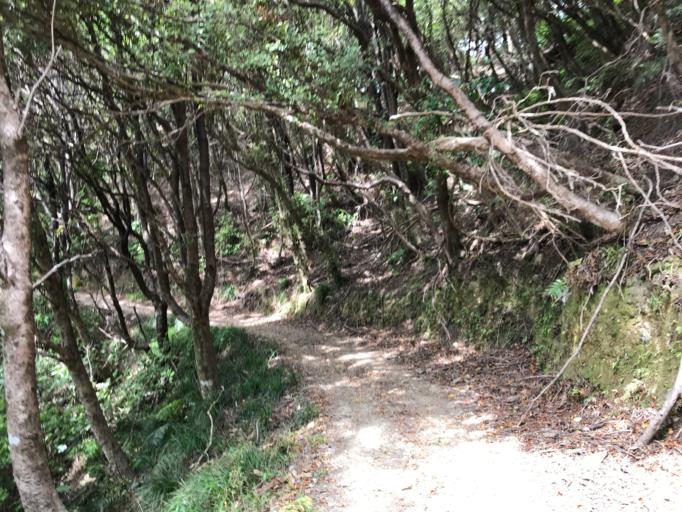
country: NZ
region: Marlborough
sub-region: Marlborough District
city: Picton
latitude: -41.1194
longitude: 174.2017
